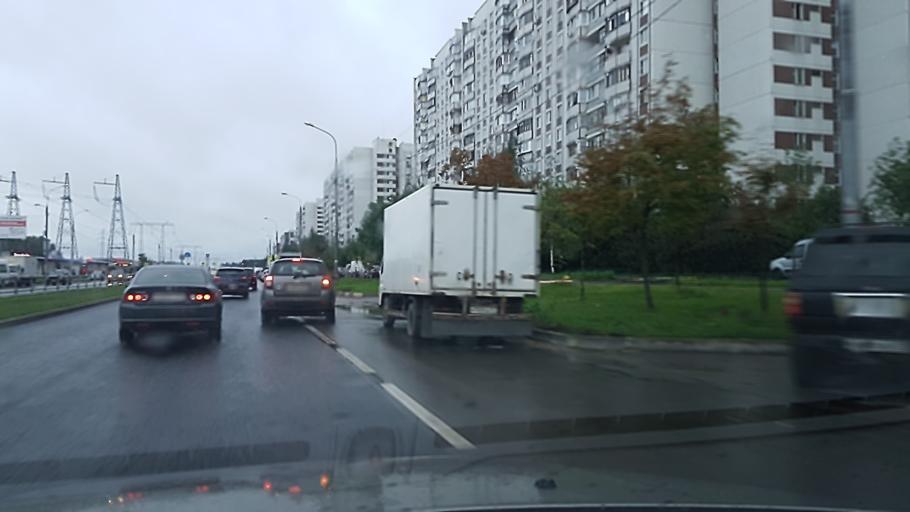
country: RU
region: Moskovskaya
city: Andreyevka
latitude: 55.9785
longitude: 37.1487
